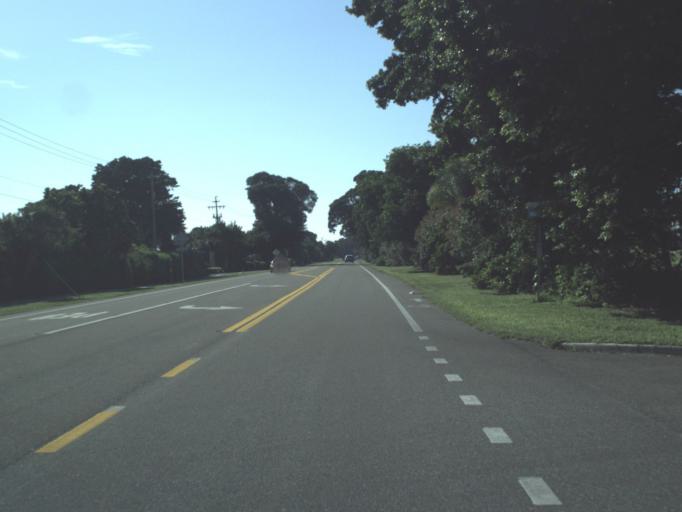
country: US
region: Florida
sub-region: Sarasota County
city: Siesta Key
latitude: 27.3456
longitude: -82.6027
